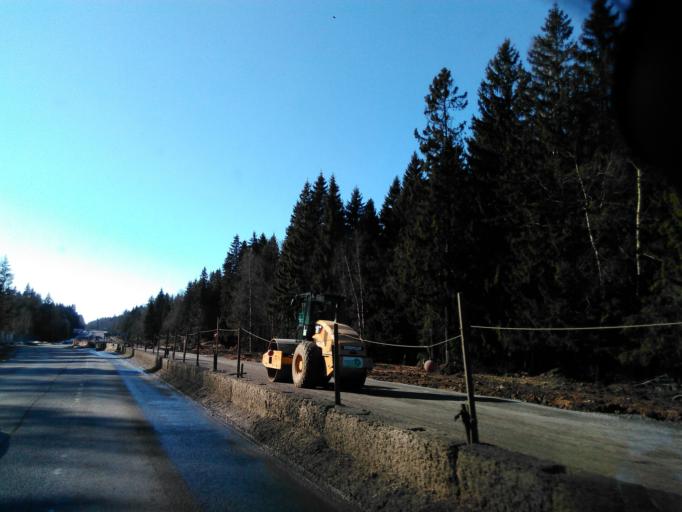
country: RU
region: Moskovskaya
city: Yermolino
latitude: 56.1382
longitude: 37.4851
